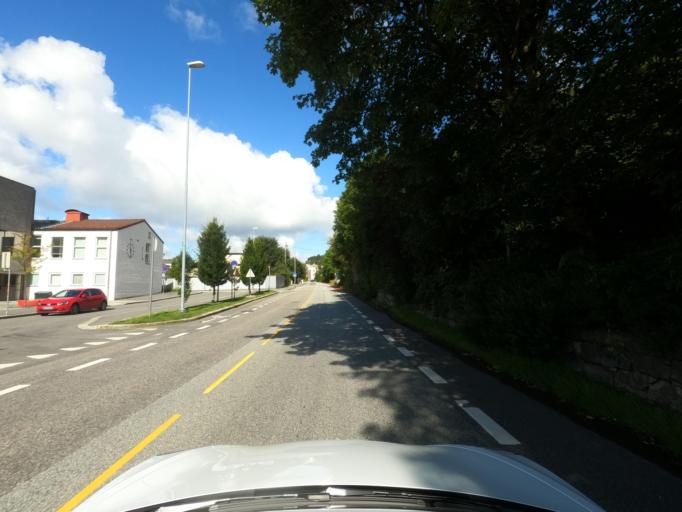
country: NO
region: Hordaland
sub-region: Bergen
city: Bergen
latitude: 60.4261
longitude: 5.2993
